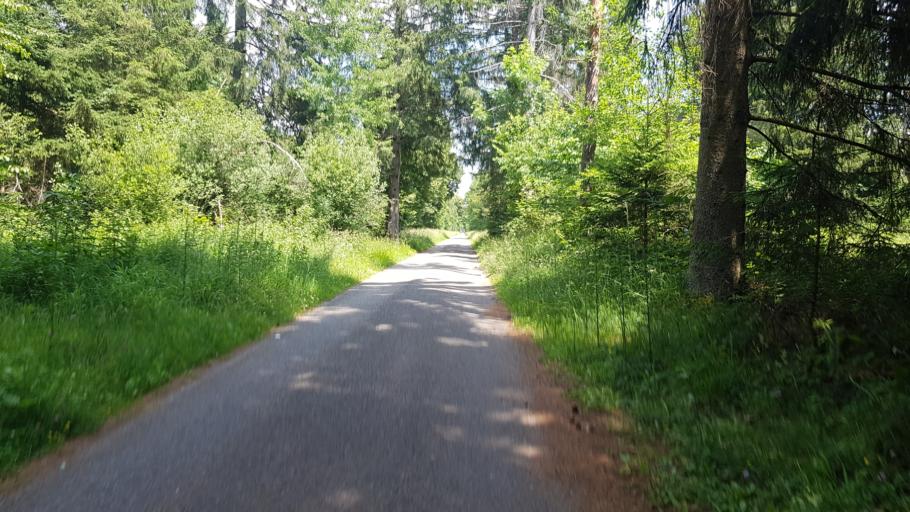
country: DE
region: Bavaria
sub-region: Upper Bavaria
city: Neuried
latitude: 48.0543
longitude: 11.4394
